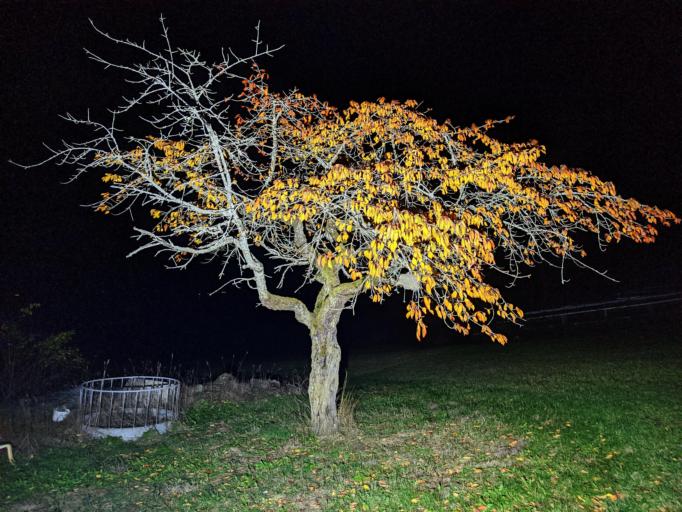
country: NO
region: Sogn og Fjordane
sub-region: Vik
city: Vikoyri
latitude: 61.1696
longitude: 6.6432
